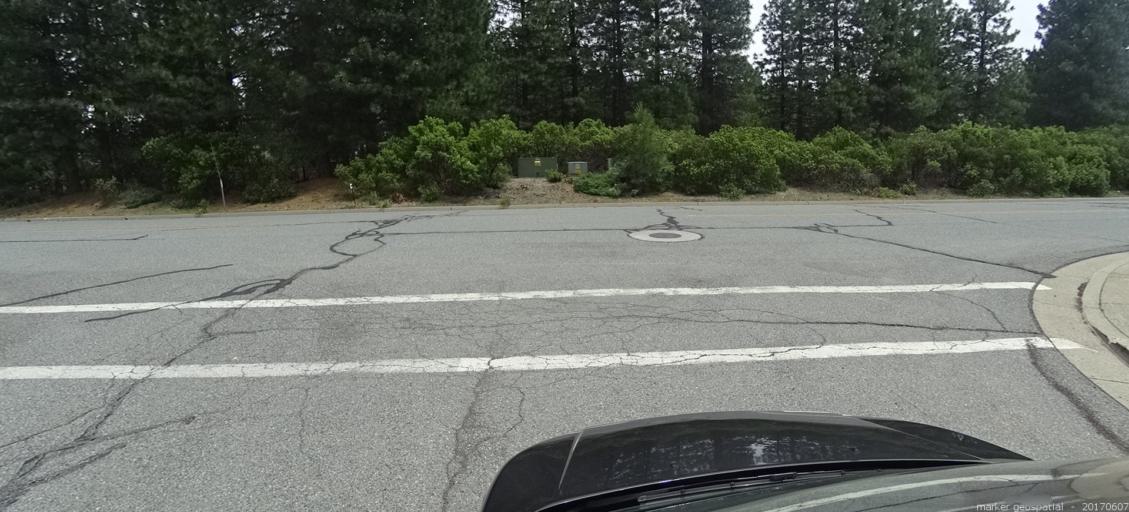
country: US
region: California
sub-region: Siskiyou County
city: Mount Shasta
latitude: 41.2904
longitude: -122.3170
